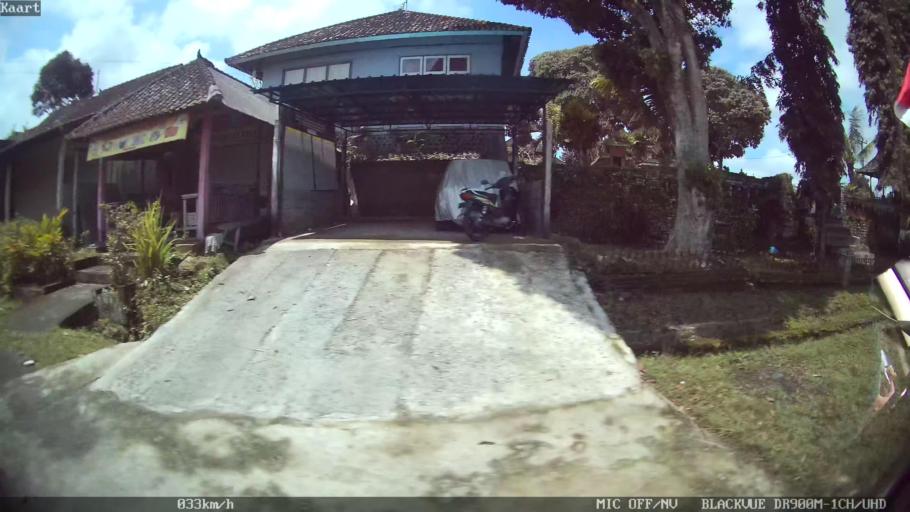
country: ID
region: Bali
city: Banjar Kelodan
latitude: -8.4989
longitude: 115.3676
